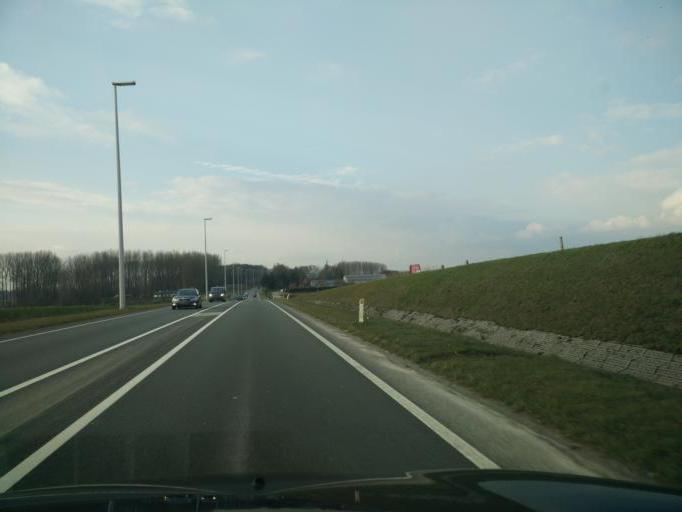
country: BE
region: Flanders
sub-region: Provincie Oost-Vlaanderen
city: Zottegem
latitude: 50.9072
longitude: 3.8224
